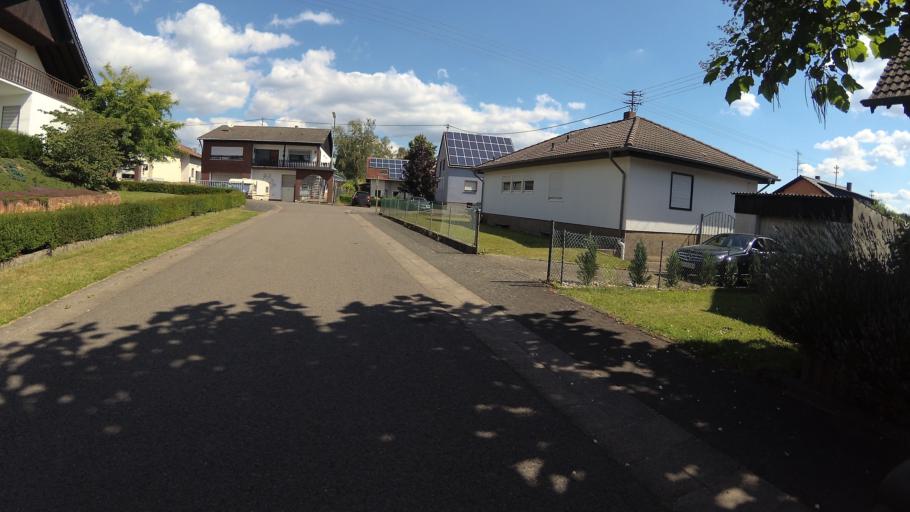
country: DE
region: Saarland
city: Weiskirchen
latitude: 49.5352
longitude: 6.8301
